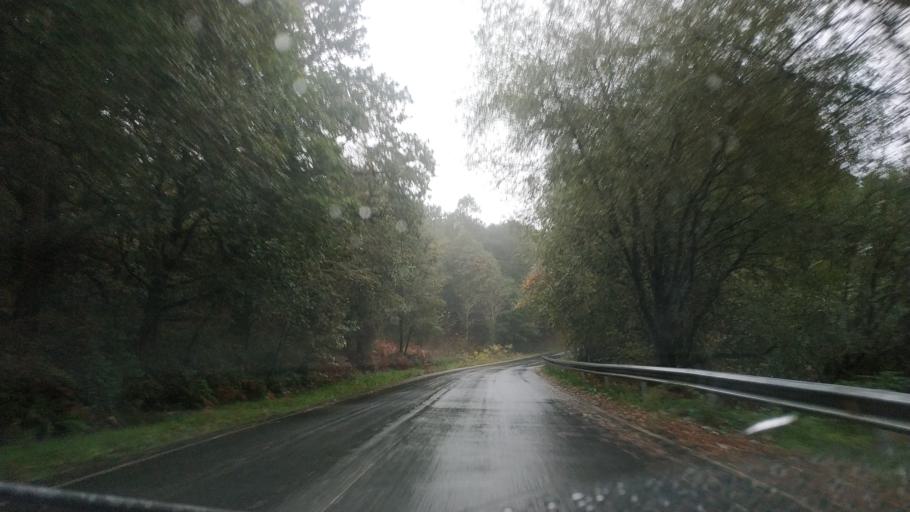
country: ES
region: Galicia
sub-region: Provincia da Coruna
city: Negreira
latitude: 42.9075
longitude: -8.7473
